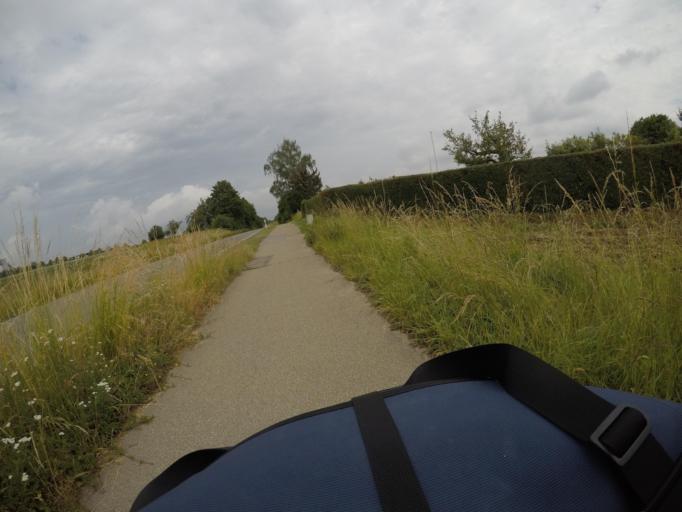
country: DE
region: Baden-Wuerttemberg
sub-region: Regierungsbezirk Stuttgart
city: Ditzingen
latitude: 48.8132
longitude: 9.0693
